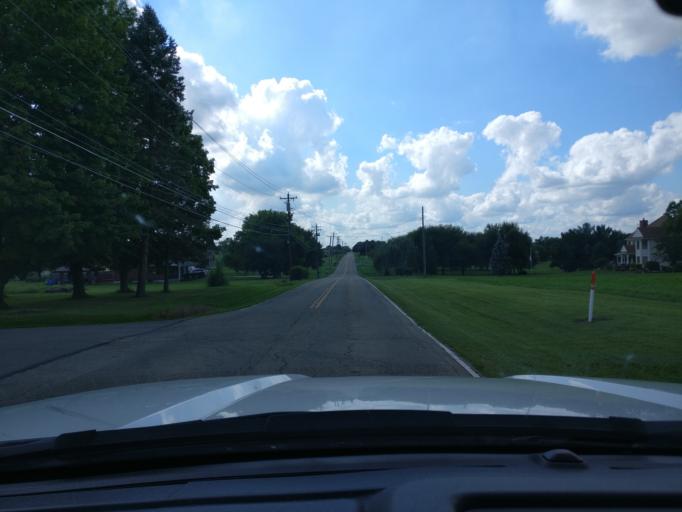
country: US
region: Ohio
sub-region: Warren County
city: Springboro
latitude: 39.5030
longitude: -84.2008
